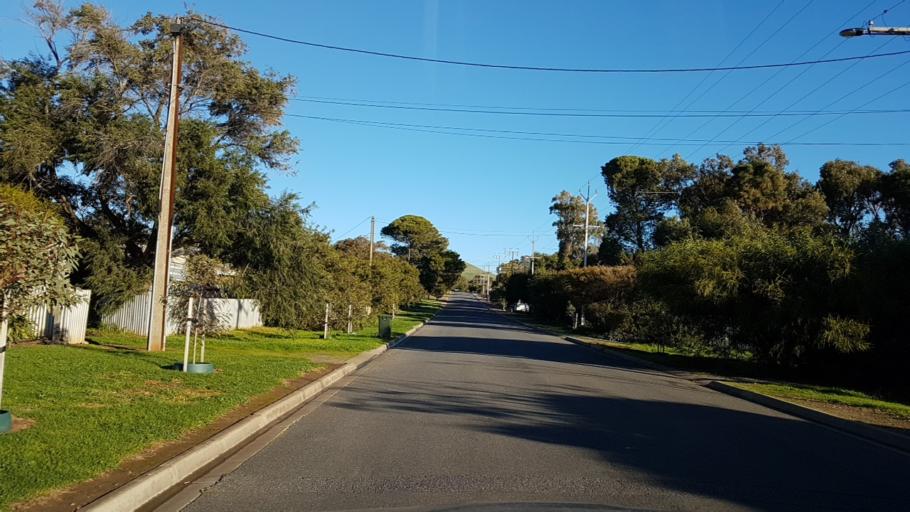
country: AU
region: South Australia
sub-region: Onkaparinga
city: Port Willunga
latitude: -35.3307
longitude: 138.4505
